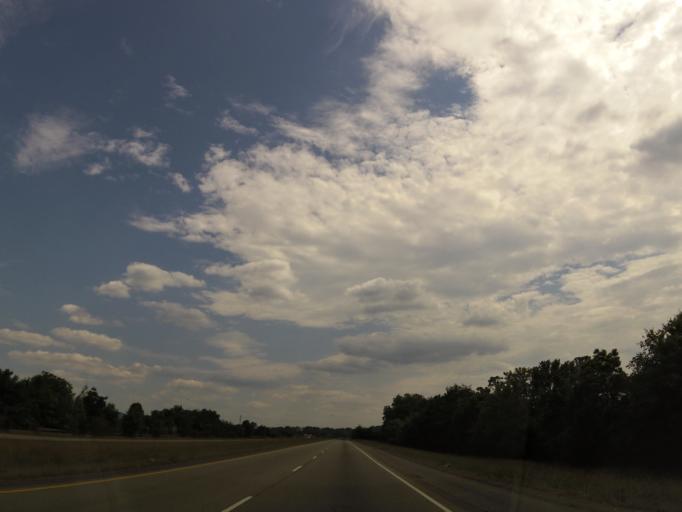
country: US
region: Tennessee
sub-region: Marion County
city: South Pittsburg
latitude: 35.0072
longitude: -85.7020
